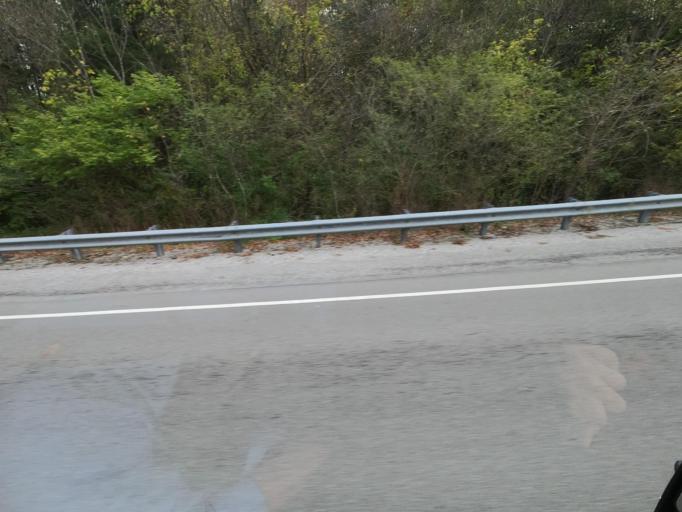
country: US
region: Tennessee
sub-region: Cheatham County
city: Pegram
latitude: 36.0854
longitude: -87.0256
